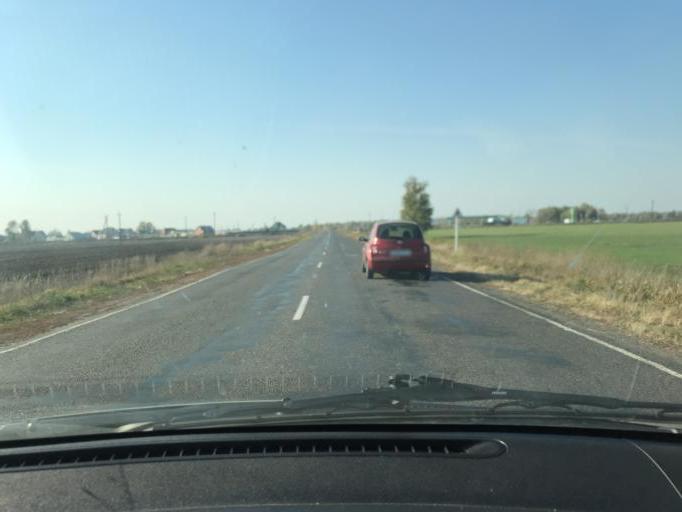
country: BY
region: Brest
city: Davyd-Haradok
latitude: 52.0693
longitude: 27.2461
